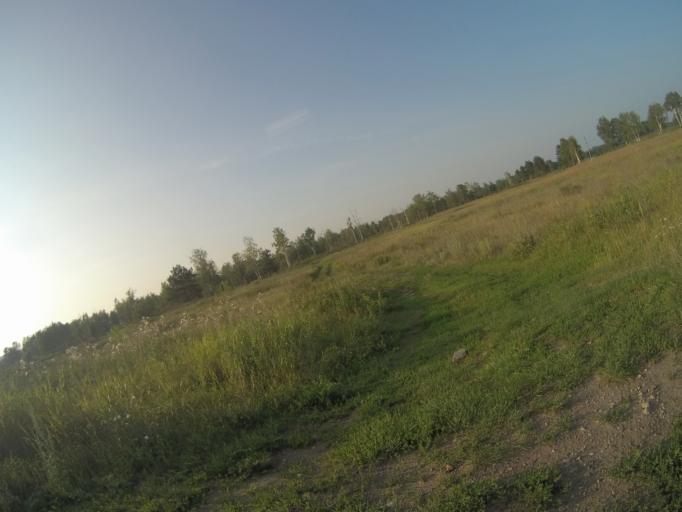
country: RU
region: Vladimir
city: Kommunar
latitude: 56.1162
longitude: 40.4333
